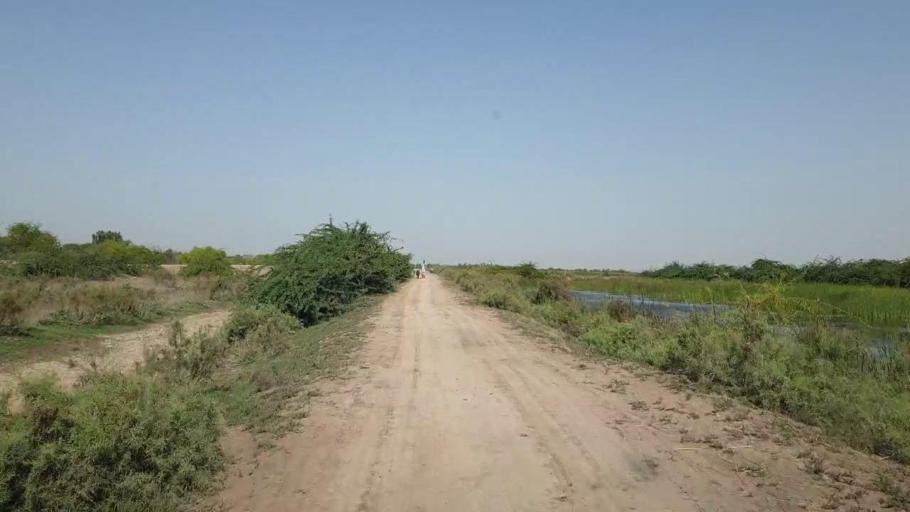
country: PK
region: Sindh
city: Tando Bago
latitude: 24.6587
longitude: 69.0695
